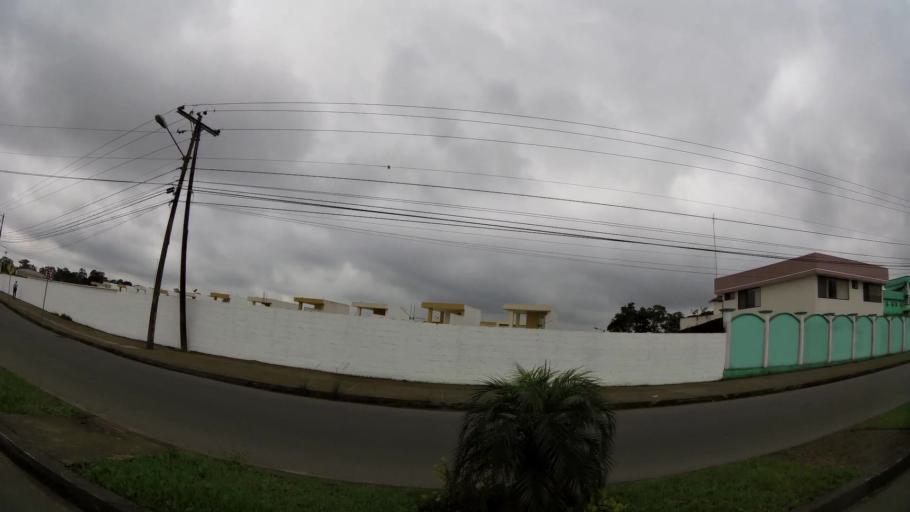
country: EC
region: Santo Domingo de los Tsachilas
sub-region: Canton Santo Domingo de los Colorados
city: Santo Domingo de los Colorados
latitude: -0.2598
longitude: -79.1420
